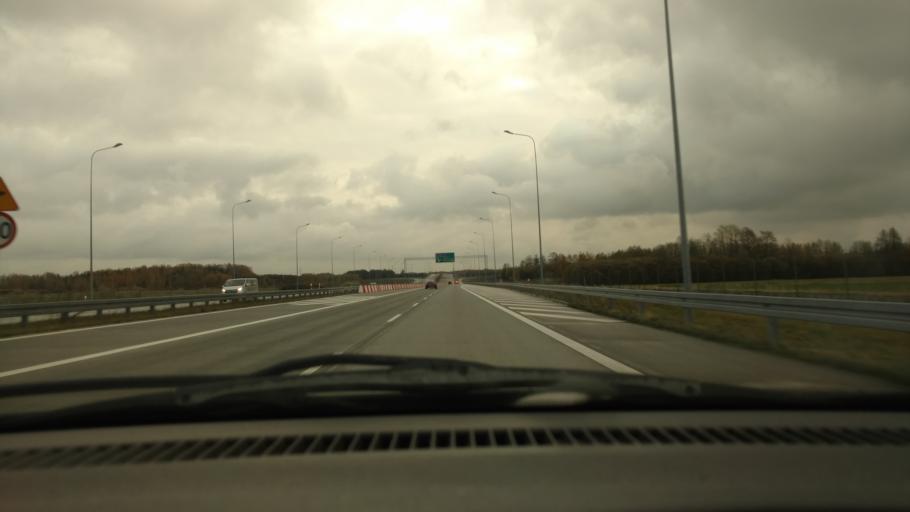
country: PL
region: Lodz Voivodeship
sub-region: Powiat lodzki wschodni
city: Tuszyn
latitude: 51.6408
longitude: 19.5572
